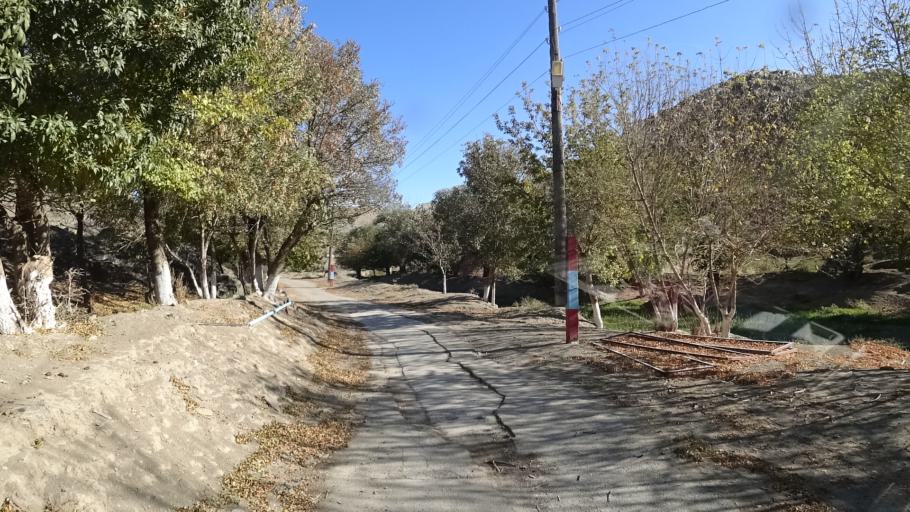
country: UZ
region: Navoiy
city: Karmana Shahri
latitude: 40.2958
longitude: 65.6046
